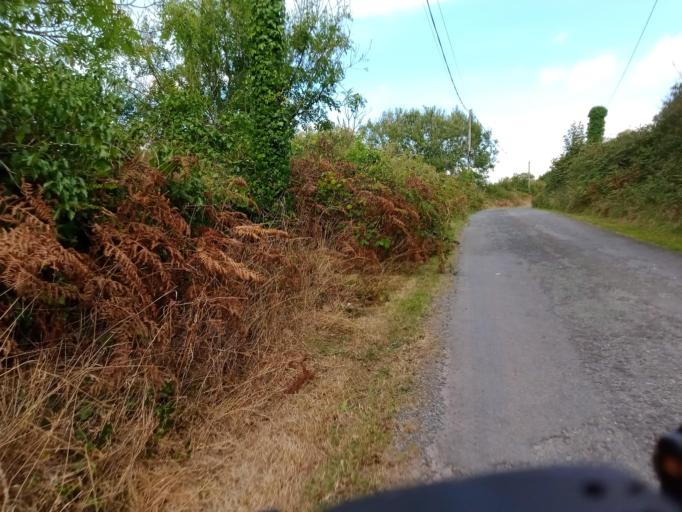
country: IE
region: Munster
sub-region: Waterford
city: Dungarvan
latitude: 52.1149
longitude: -7.5060
